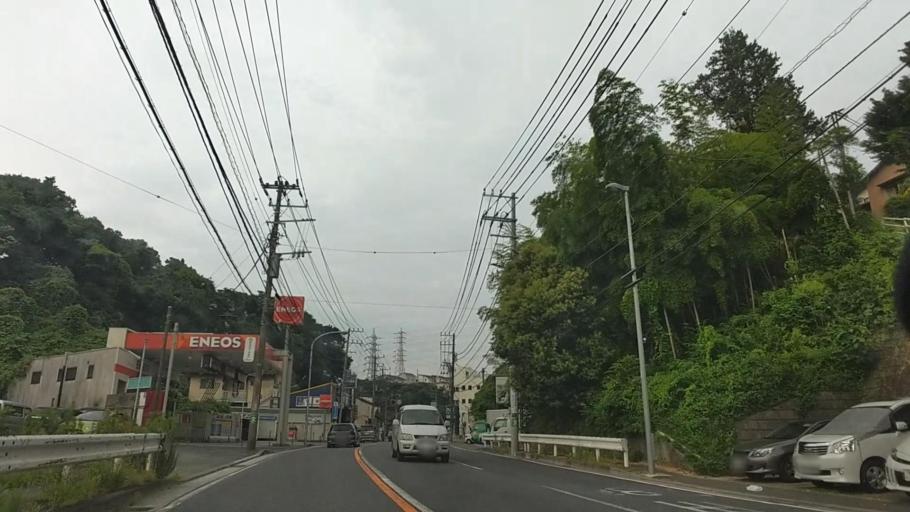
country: JP
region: Kanagawa
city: Yokohama
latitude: 35.4421
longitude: 139.5760
